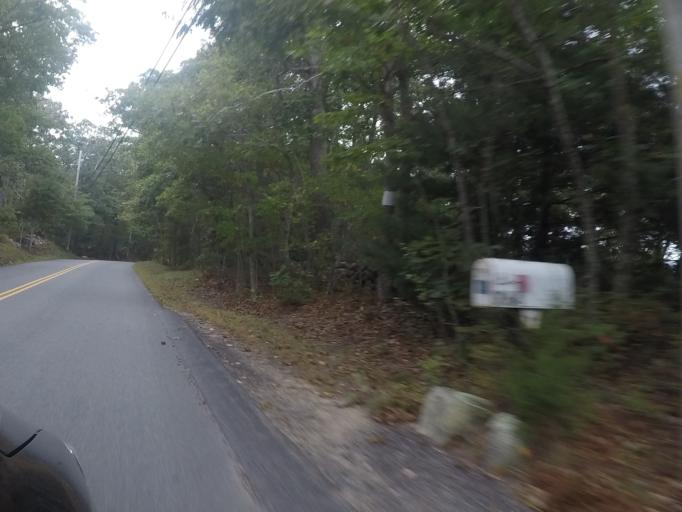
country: US
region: Massachusetts
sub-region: Bristol County
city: Smith Mills
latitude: 41.5658
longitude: -71.0000
